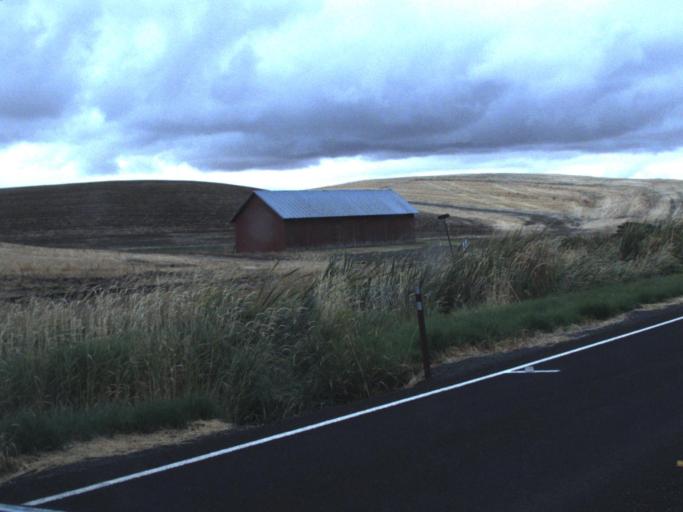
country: US
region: Washington
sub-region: Whitman County
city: Colfax
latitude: 47.1796
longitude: -117.2935
